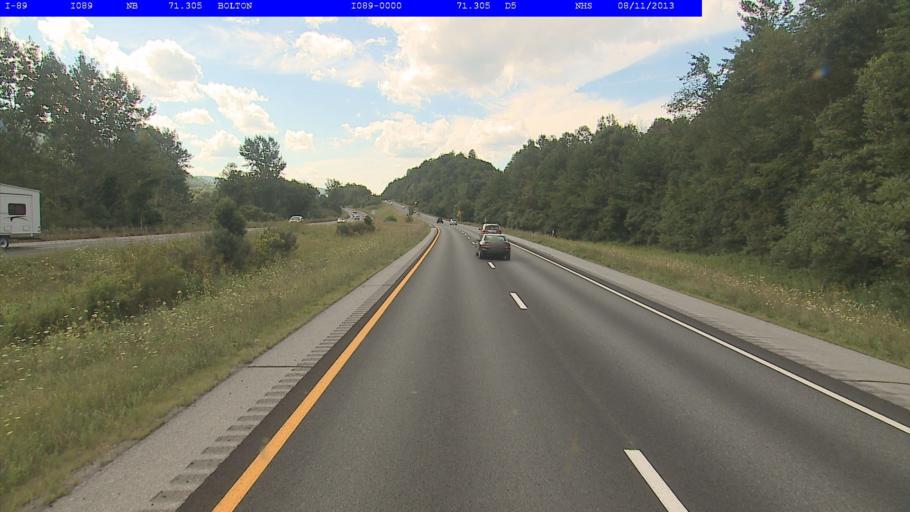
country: US
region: Vermont
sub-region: Washington County
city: Waterbury
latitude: 44.3772
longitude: -72.8925
